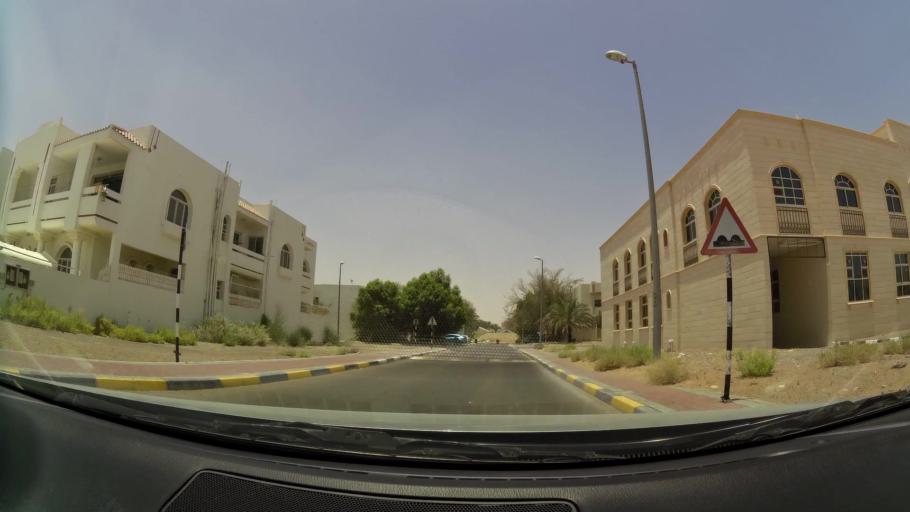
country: OM
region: Al Buraimi
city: Al Buraymi
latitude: 24.2612
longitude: 55.7248
